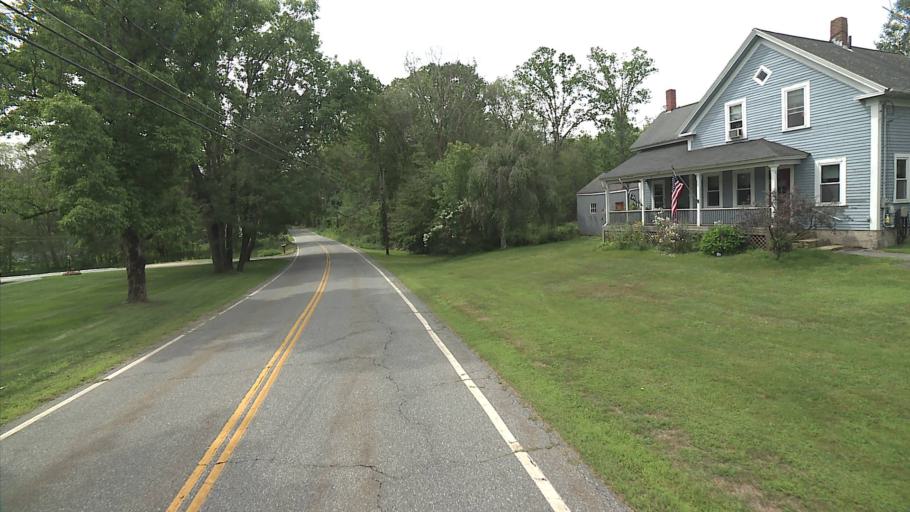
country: US
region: Massachusetts
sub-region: Worcester County
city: Webster
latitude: 42.0170
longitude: -71.8450
